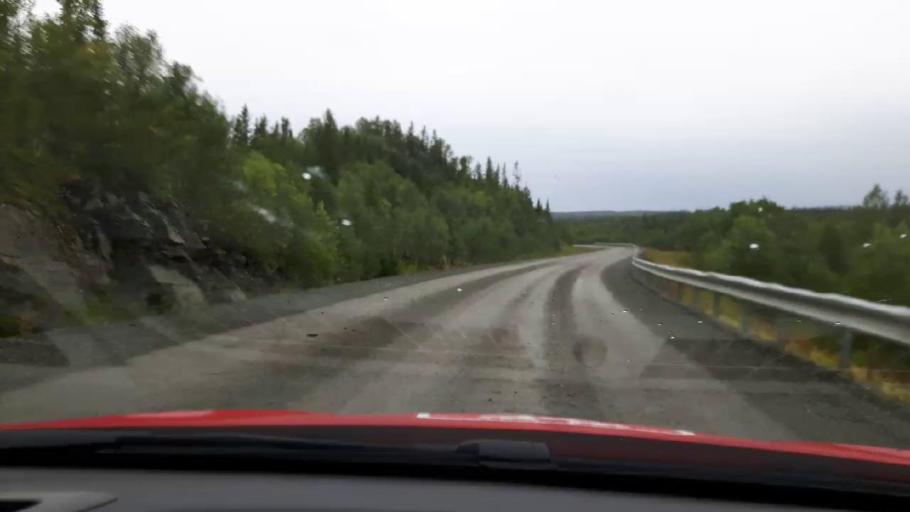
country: NO
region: Nord-Trondelag
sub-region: Meraker
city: Meraker
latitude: 63.5750
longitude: 12.2802
